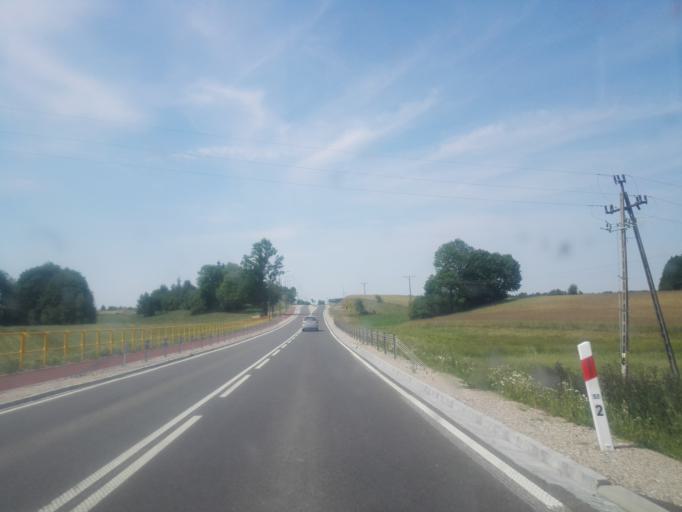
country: PL
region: Podlasie
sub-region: Powiat sejnenski
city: Sejny
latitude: 54.1086
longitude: 23.2859
